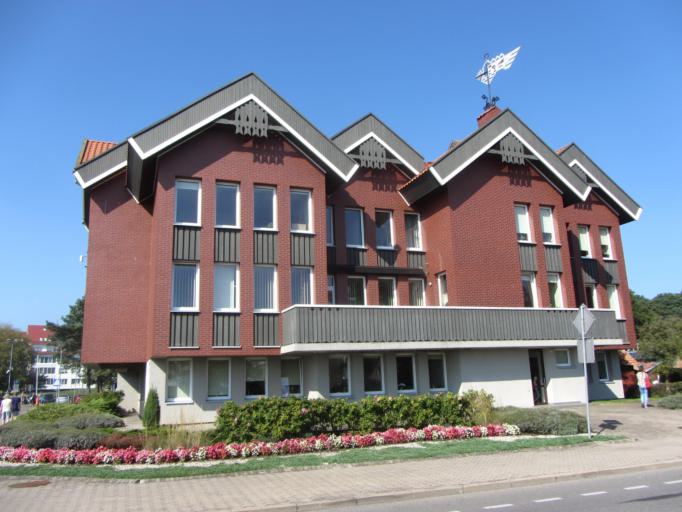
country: LT
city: Nida
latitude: 55.3035
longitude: 21.0070
